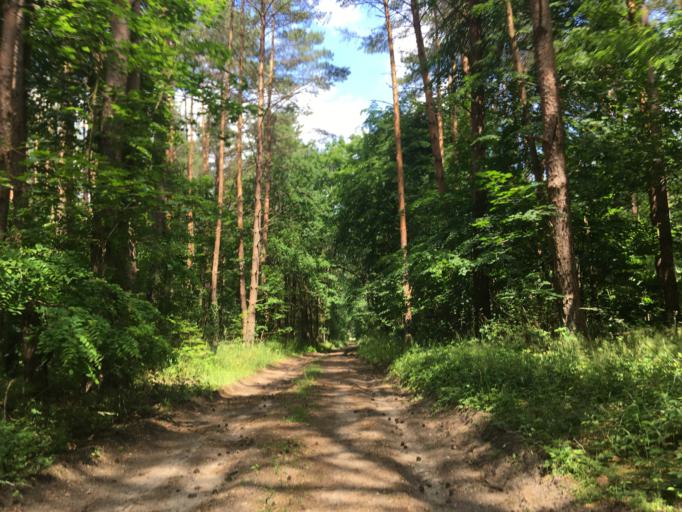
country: DE
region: Brandenburg
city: Rehfelde
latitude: 52.5460
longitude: 13.9123
